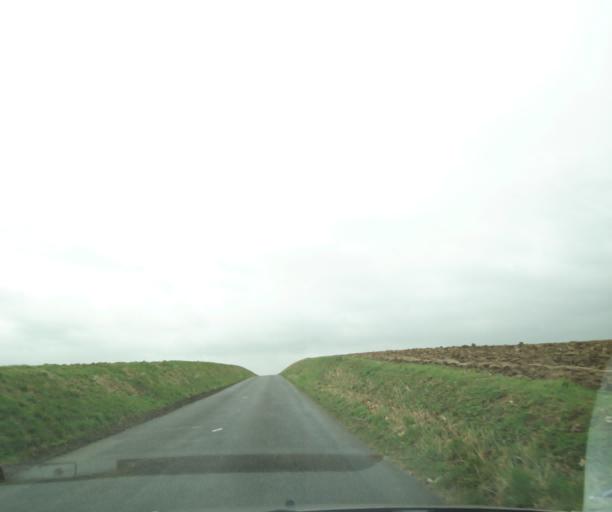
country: FR
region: Picardie
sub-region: Departement de l'Oise
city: Crisolles
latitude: 49.6039
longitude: 3.0084
